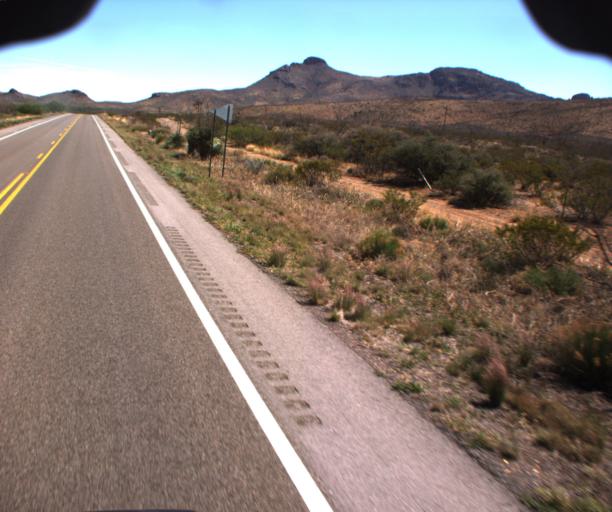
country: US
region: Arizona
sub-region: Cochise County
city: Douglas
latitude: 31.4482
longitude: -109.4678
